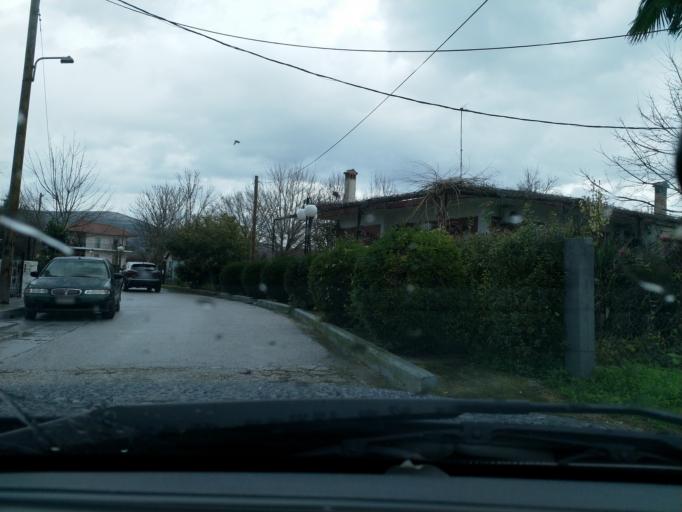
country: GR
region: Thessaly
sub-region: Trikala
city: Taxiarches
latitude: 39.5462
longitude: 21.8954
